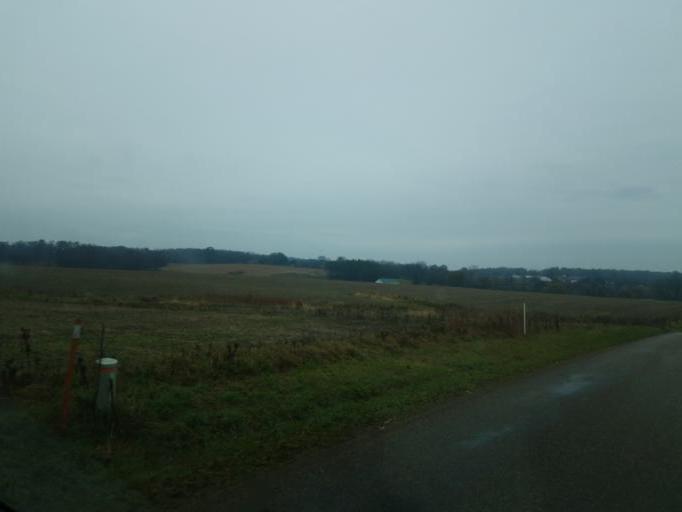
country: US
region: Ohio
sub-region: Knox County
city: Fredericktown
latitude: 40.5574
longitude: -82.5736
